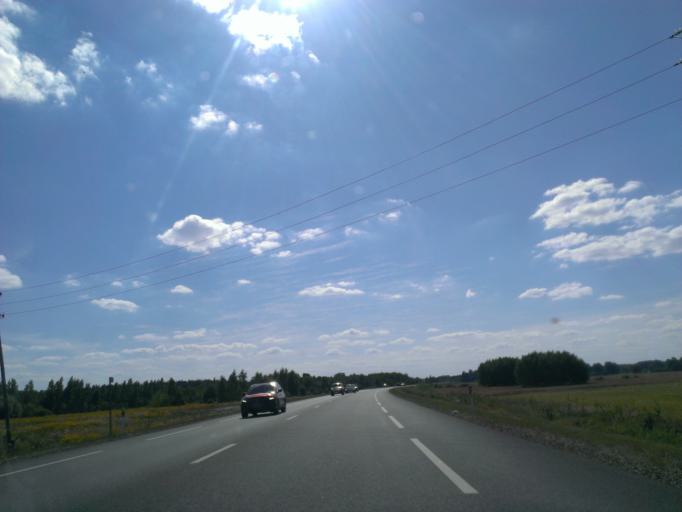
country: LV
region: Adazi
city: Adazi
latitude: 57.1138
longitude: 24.3224
